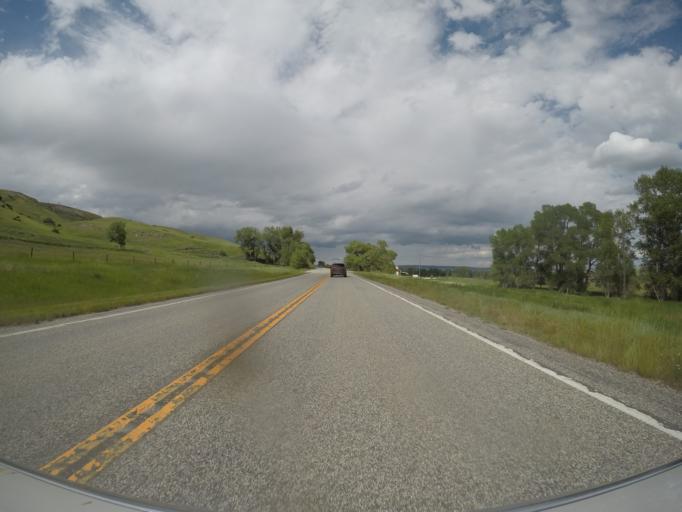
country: US
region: Montana
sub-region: Sweet Grass County
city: Big Timber
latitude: 45.8110
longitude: -109.9600
